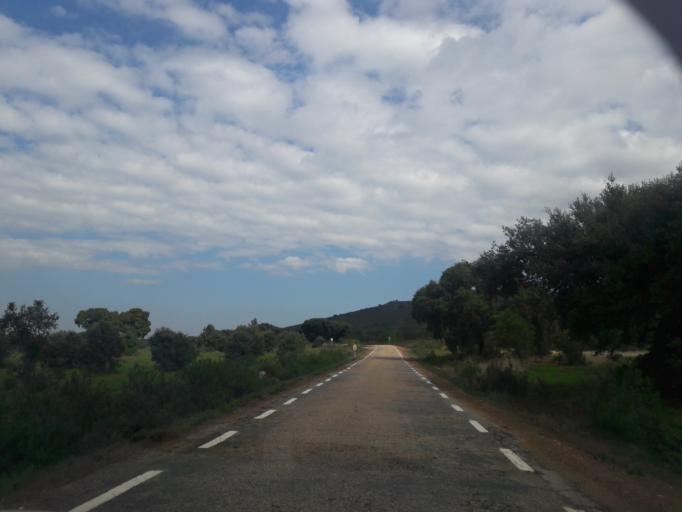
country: ES
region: Castille and Leon
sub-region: Provincia de Salamanca
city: Serradilla del Arroyo
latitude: 40.5356
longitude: -6.3831
